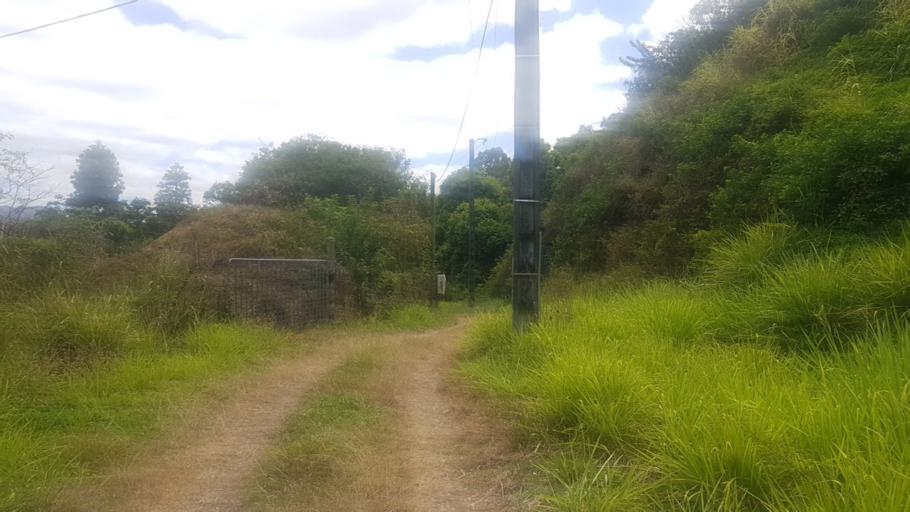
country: NC
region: South Province
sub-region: Dumbea
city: Dumbea
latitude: -22.1839
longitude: 166.4797
